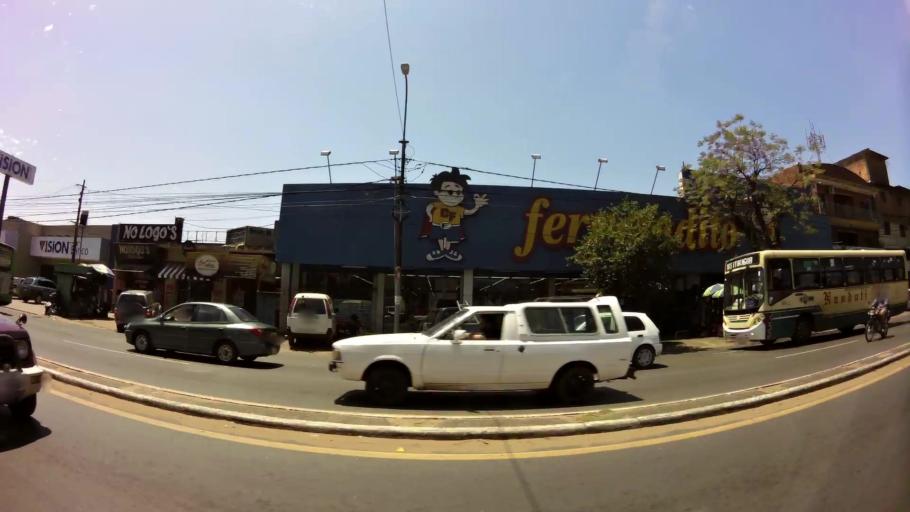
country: PY
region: Central
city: Fernando de la Mora
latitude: -25.3232
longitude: -57.5546
